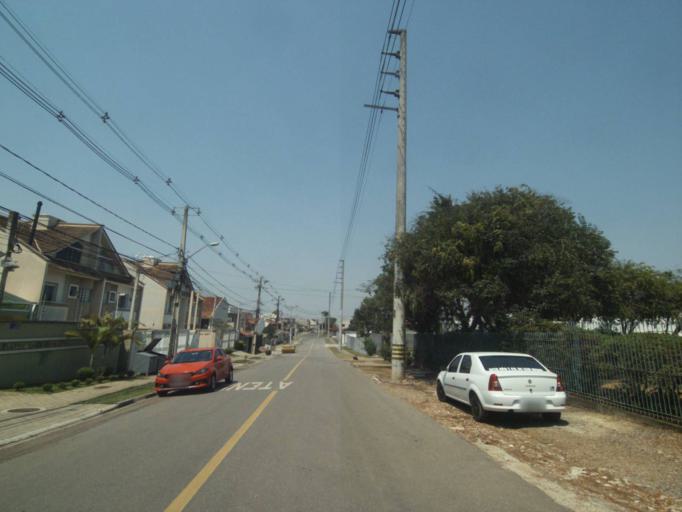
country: BR
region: Parana
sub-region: Sao Jose Dos Pinhais
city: Sao Jose dos Pinhais
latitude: -25.4999
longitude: -49.2705
